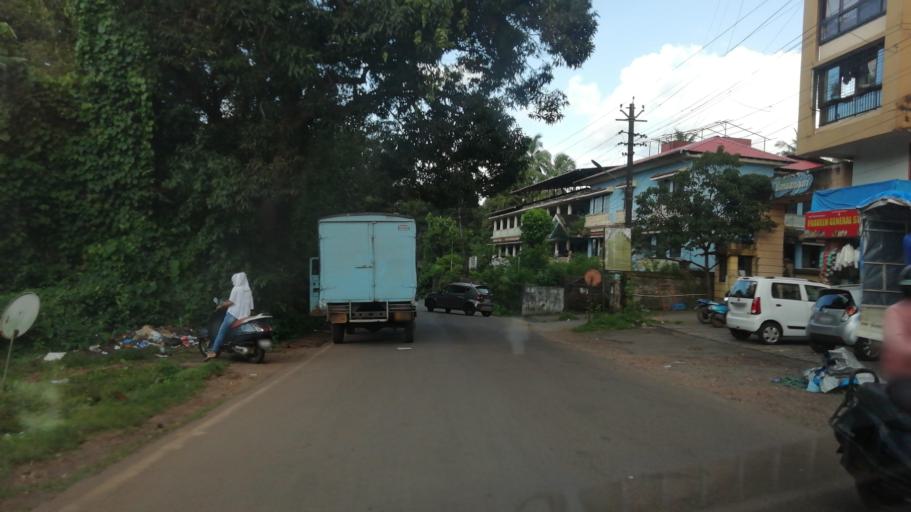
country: IN
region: Goa
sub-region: North Goa
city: Queula
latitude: 15.3928
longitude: 74.0003
